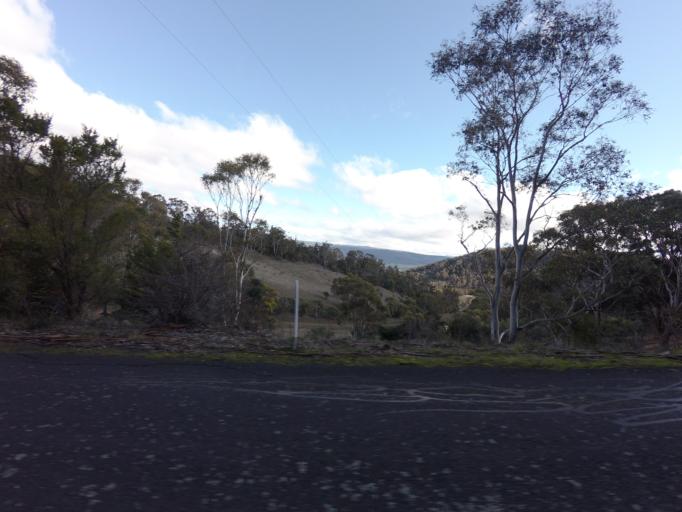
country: AU
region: Tasmania
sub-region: Derwent Valley
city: New Norfolk
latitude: -42.7340
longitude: 147.0324
